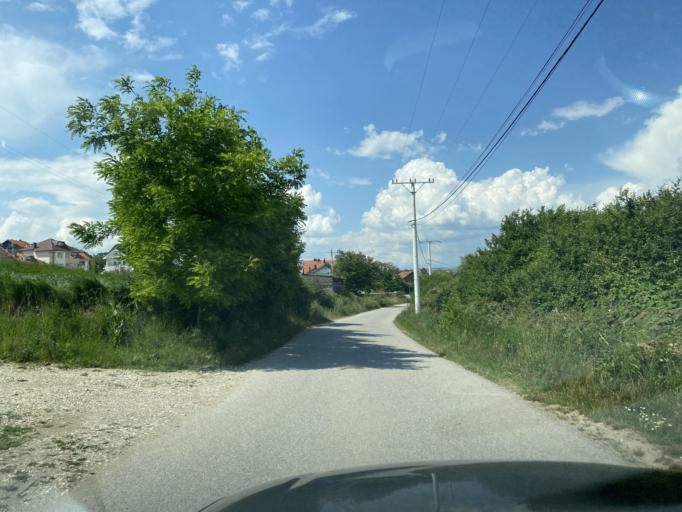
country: XK
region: Pristina
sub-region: Podujevo
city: Podujeva
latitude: 42.8672
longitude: 21.1764
